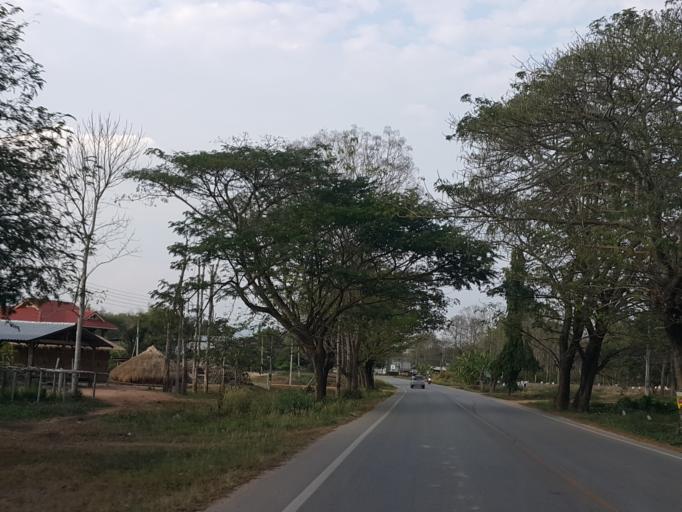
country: TH
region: Lampang
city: Lampang
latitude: 18.4951
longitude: 99.4720
